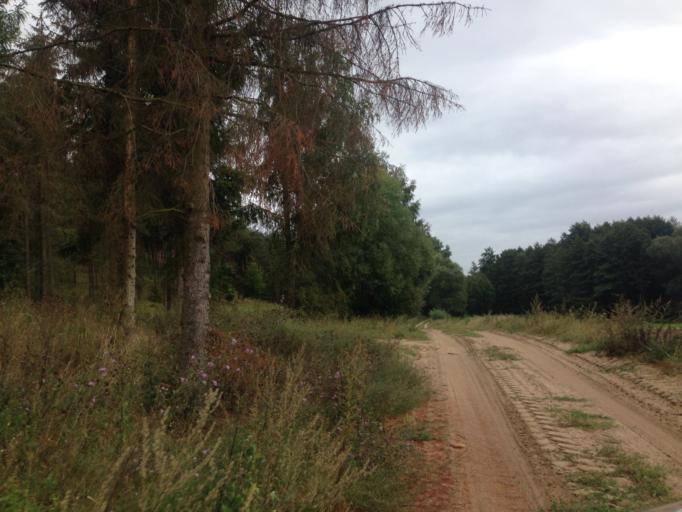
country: PL
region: Kujawsko-Pomorskie
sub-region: Powiat brodnicki
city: Bartniczka
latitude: 53.2748
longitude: 19.6307
